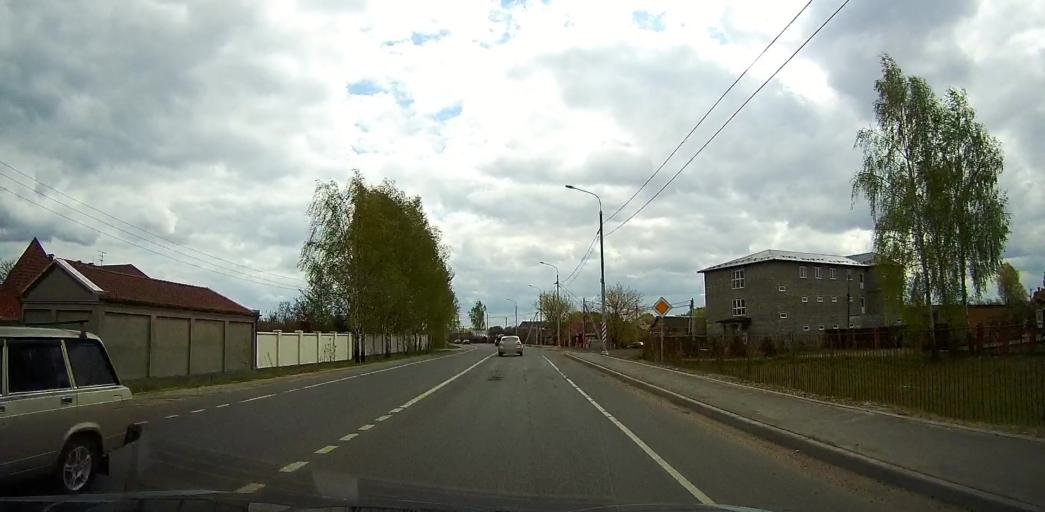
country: RU
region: Moskovskaya
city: Beloozerskiy
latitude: 55.4506
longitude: 38.4398
